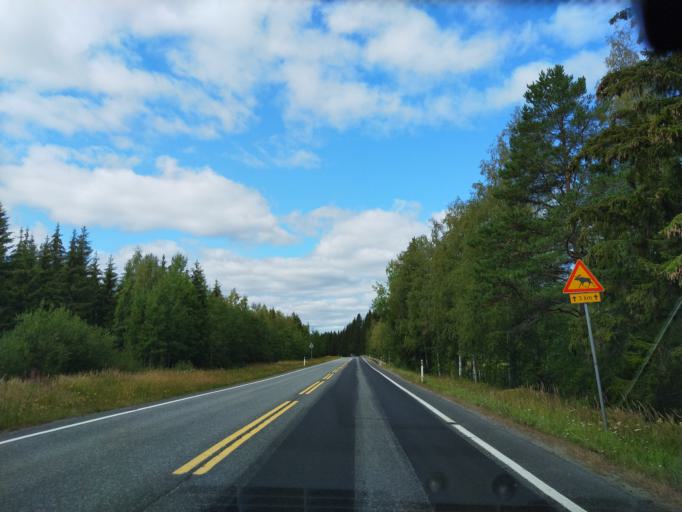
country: FI
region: Haeme
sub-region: Haemeenlinna
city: Tervakoski
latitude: 60.7428
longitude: 24.6712
